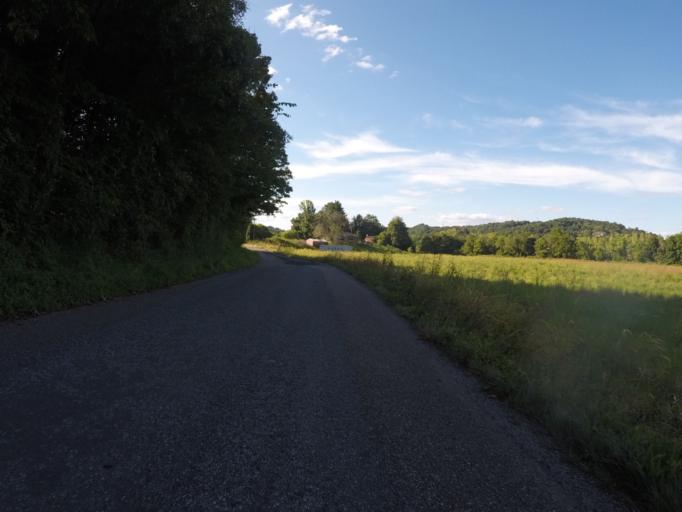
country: US
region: West Virginia
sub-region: Cabell County
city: Huntington
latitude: 38.4798
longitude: -82.4663
